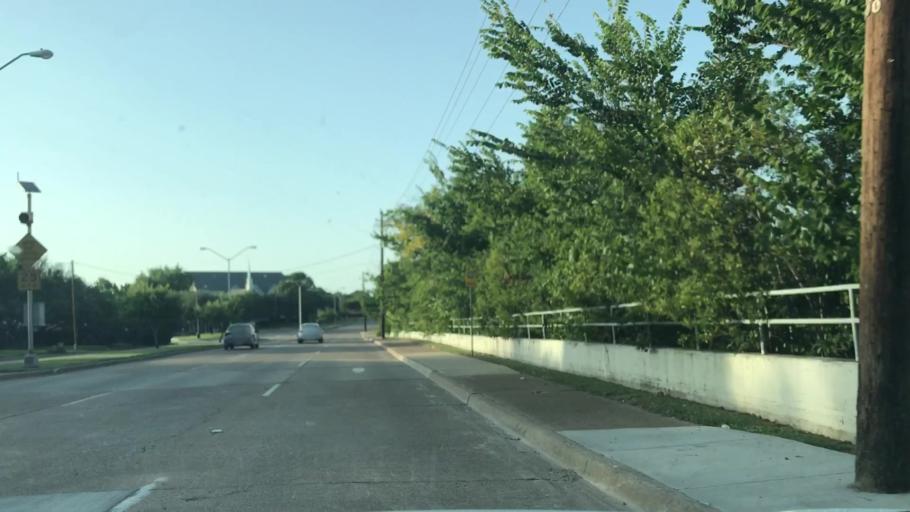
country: US
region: Texas
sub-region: Dallas County
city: Garland
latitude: 32.8691
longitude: -96.7004
